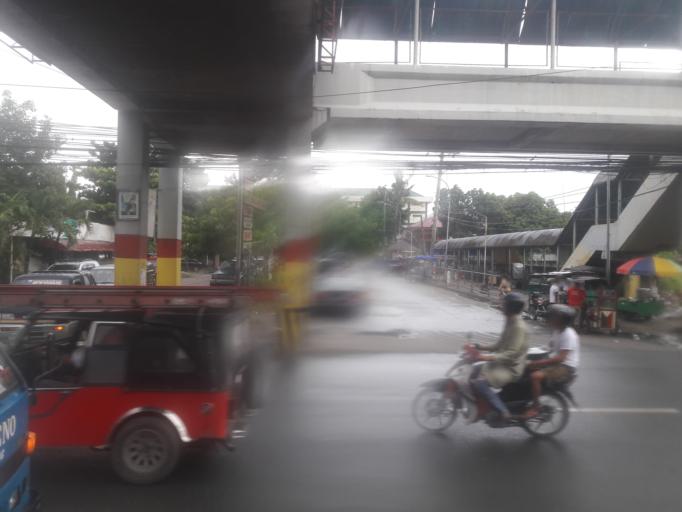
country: PH
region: Calabarzon
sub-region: Province of Cavite
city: Imus
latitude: 14.4293
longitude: 120.9453
